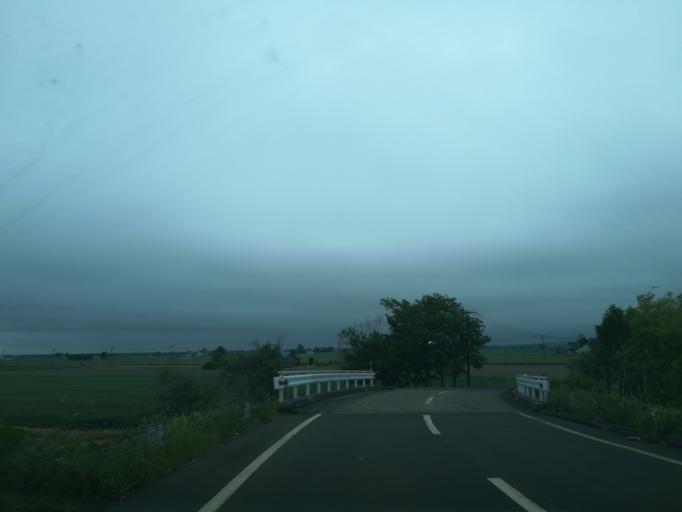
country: JP
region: Hokkaido
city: Iwamizawa
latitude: 43.1301
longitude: 141.6985
